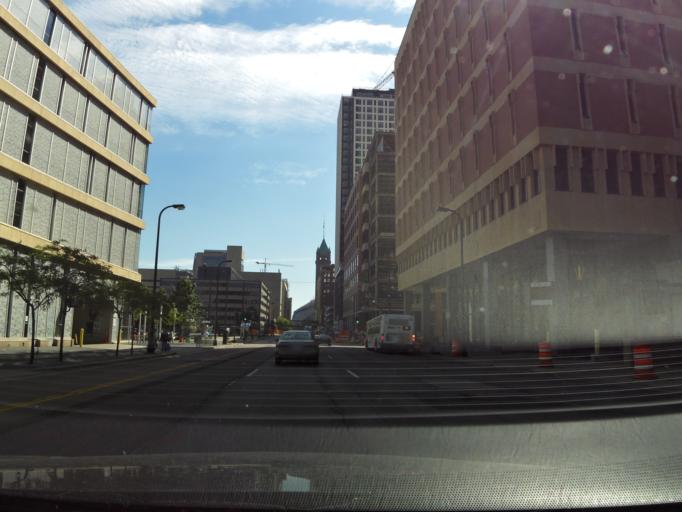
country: US
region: Minnesota
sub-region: Hennepin County
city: Minneapolis
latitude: 44.9802
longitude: -93.2707
